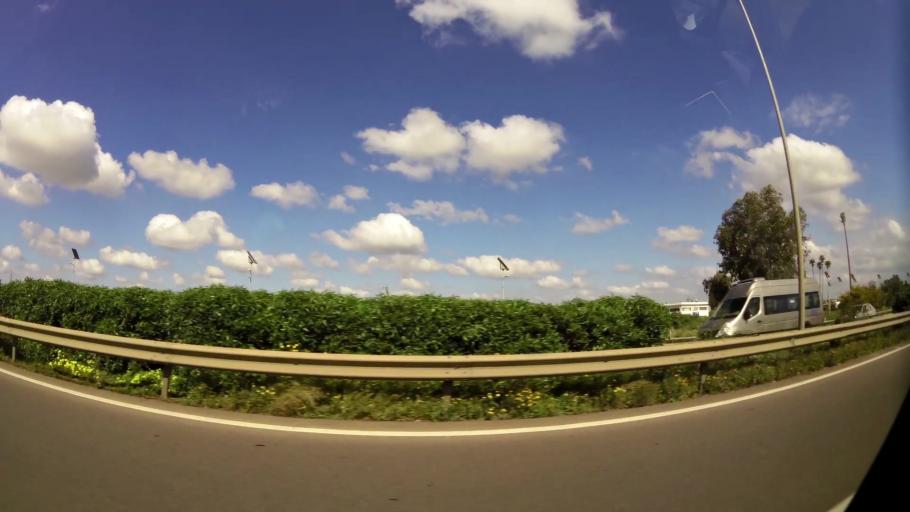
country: MA
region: Chaouia-Ouardigha
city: Nouaseur
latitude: 33.4071
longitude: -7.6249
